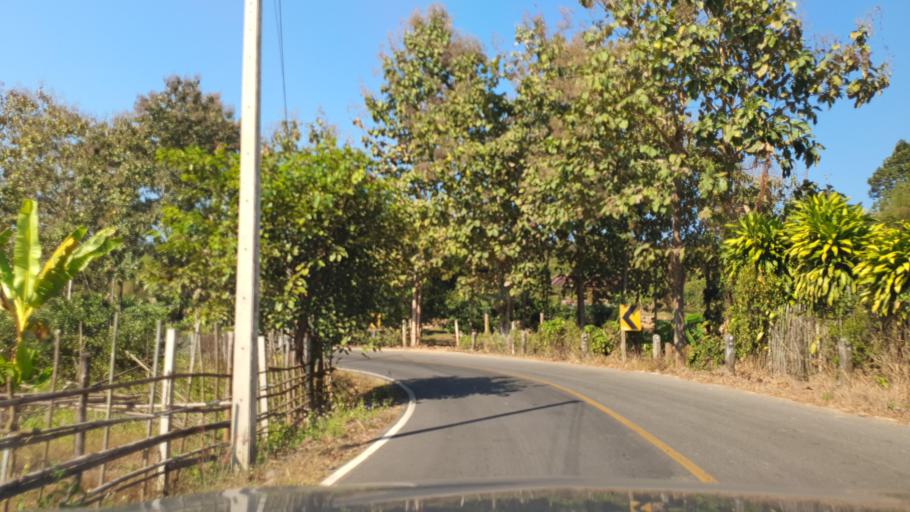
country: TH
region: Nan
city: Pua
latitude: 19.1137
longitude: 100.9102
